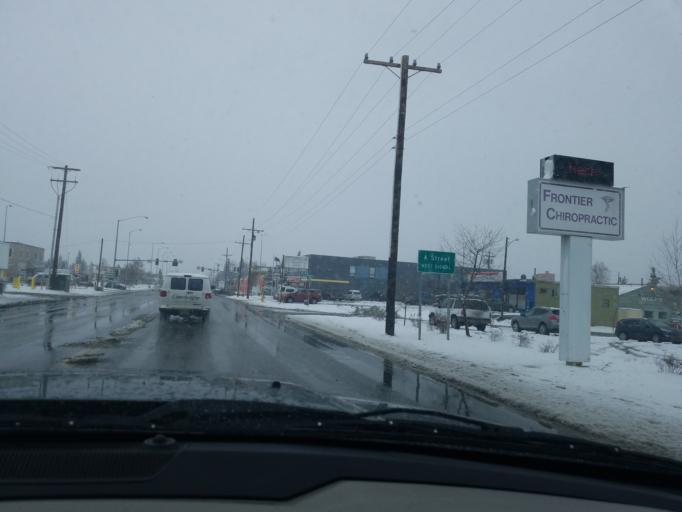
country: US
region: Alaska
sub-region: Anchorage Municipality
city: Anchorage
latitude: 61.1982
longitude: -149.8806
